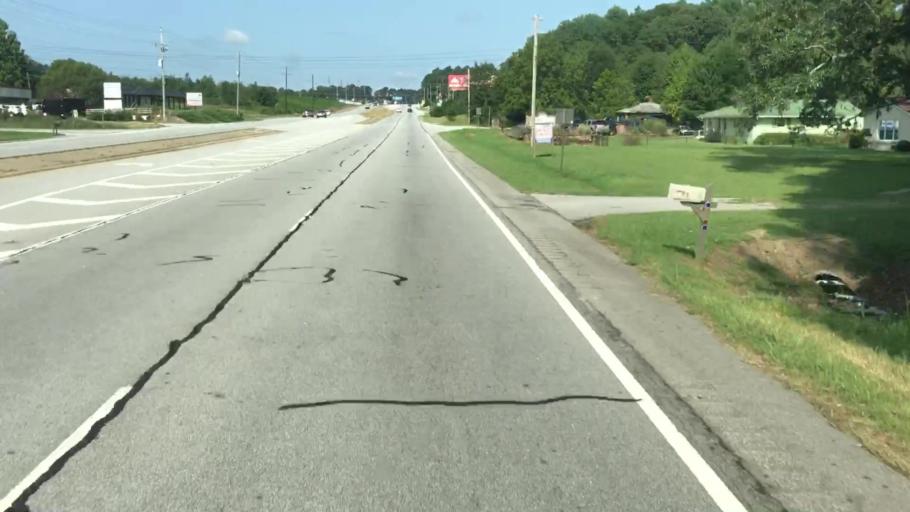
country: US
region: Georgia
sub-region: Walton County
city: Loganville
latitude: 33.8300
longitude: -83.8612
